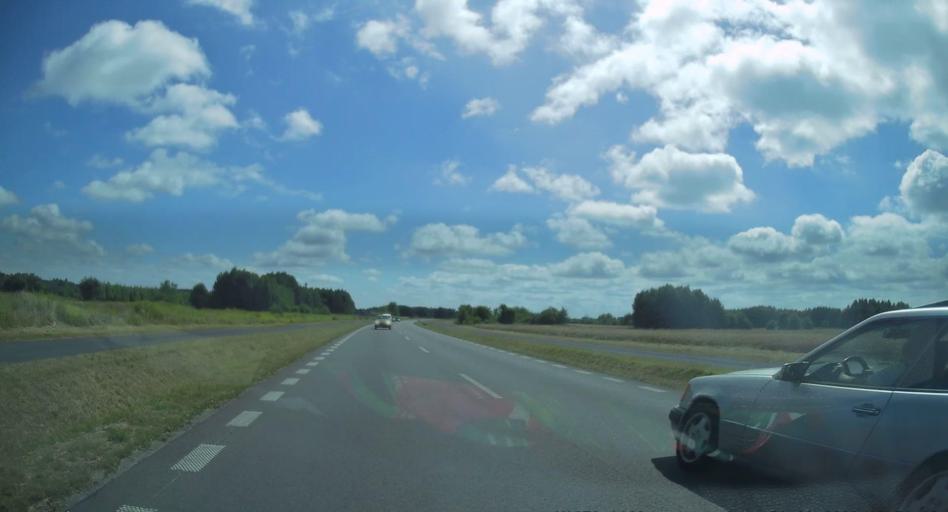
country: PL
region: Subcarpathian Voivodeship
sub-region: Powiat mielecki
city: Padew Narodowa
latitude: 50.3813
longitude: 21.4672
